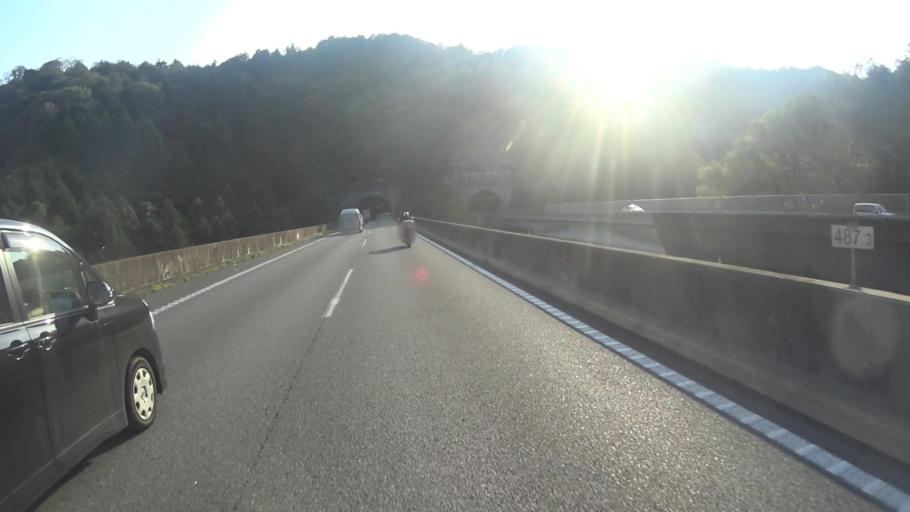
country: JP
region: Kyoto
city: Uji
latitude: 34.9198
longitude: 135.8788
